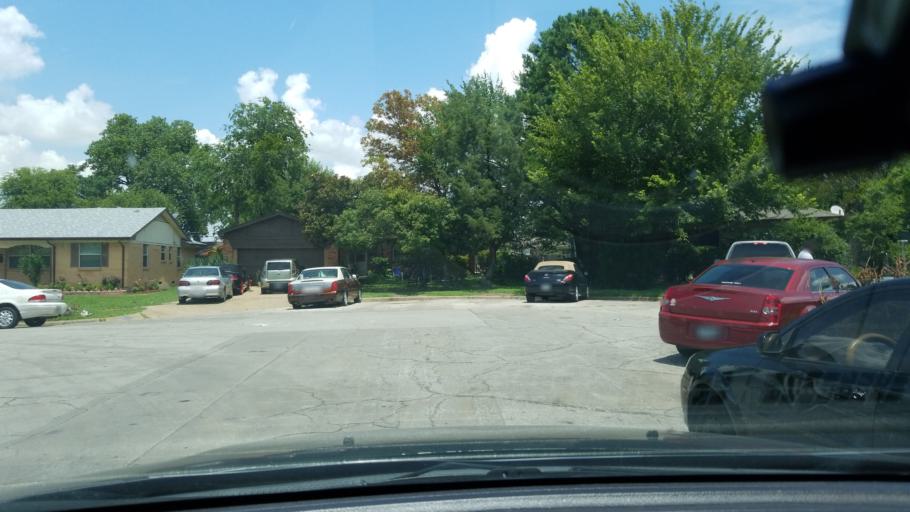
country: US
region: Texas
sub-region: Dallas County
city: Balch Springs
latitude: 32.7389
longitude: -96.6490
